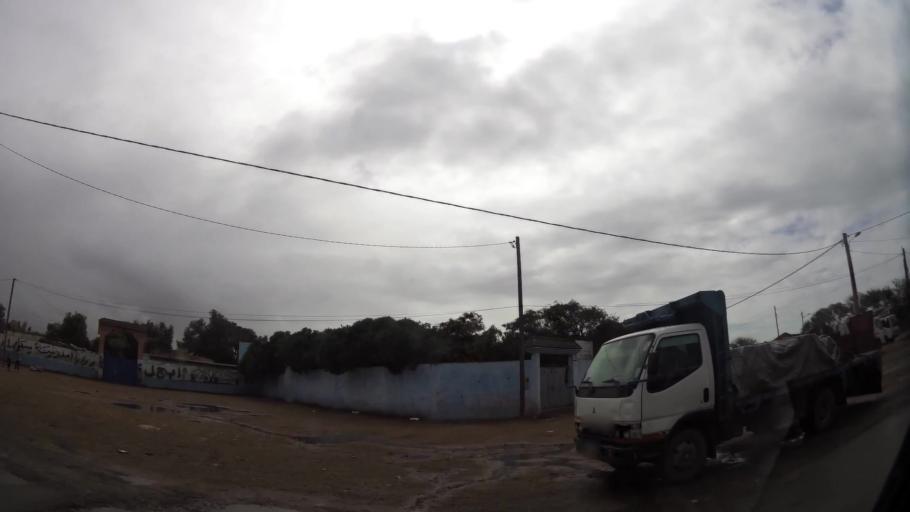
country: MA
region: Grand Casablanca
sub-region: Mediouna
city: Tit Mellil
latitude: 33.6425
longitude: -7.4774
